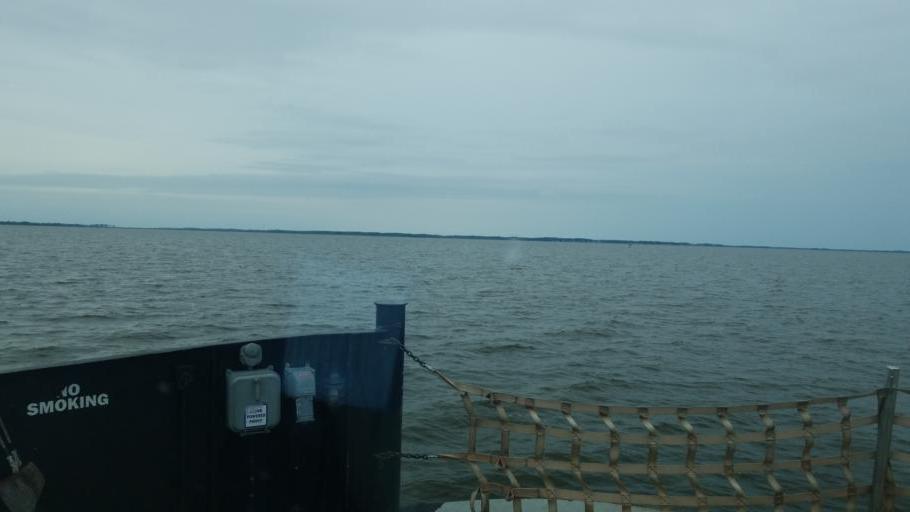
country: US
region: North Carolina
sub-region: Currituck County
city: Currituck
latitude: 36.4578
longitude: -75.9815
